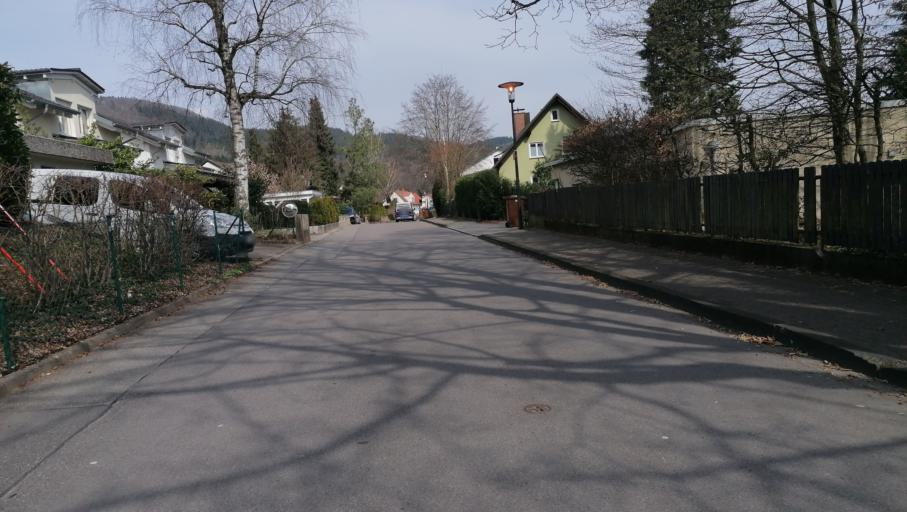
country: DE
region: Baden-Wuerttemberg
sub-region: Freiburg Region
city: Bad Sackingen
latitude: 47.5605
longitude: 7.9549
